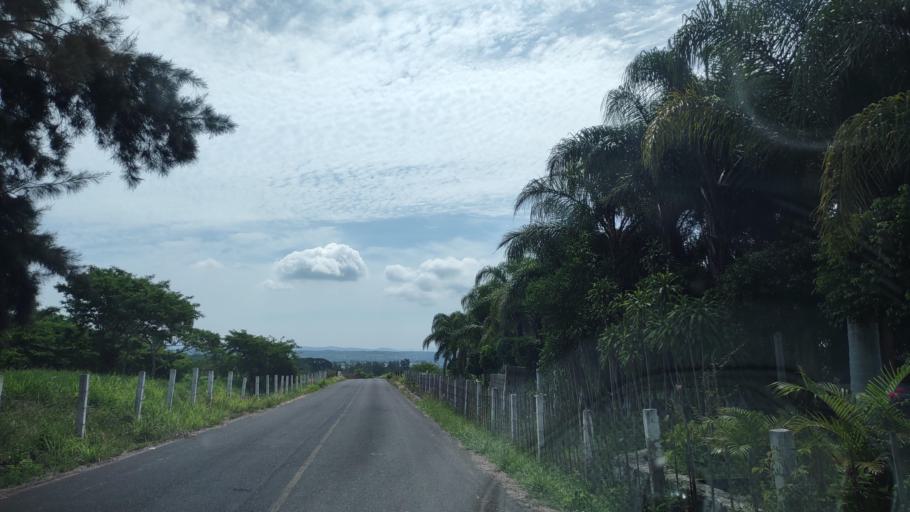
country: MX
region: Veracruz
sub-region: Emiliano Zapata
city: Dos Rios
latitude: 19.4730
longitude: -96.8281
